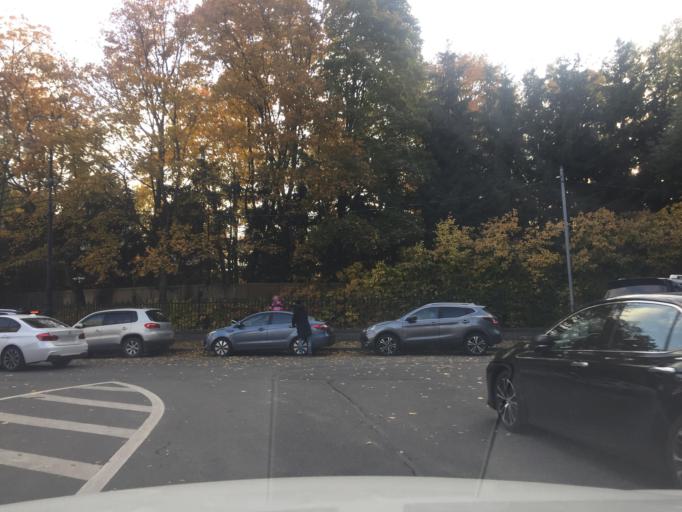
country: RU
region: St.-Petersburg
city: Novaya Derevnya
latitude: 59.9770
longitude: 30.2747
